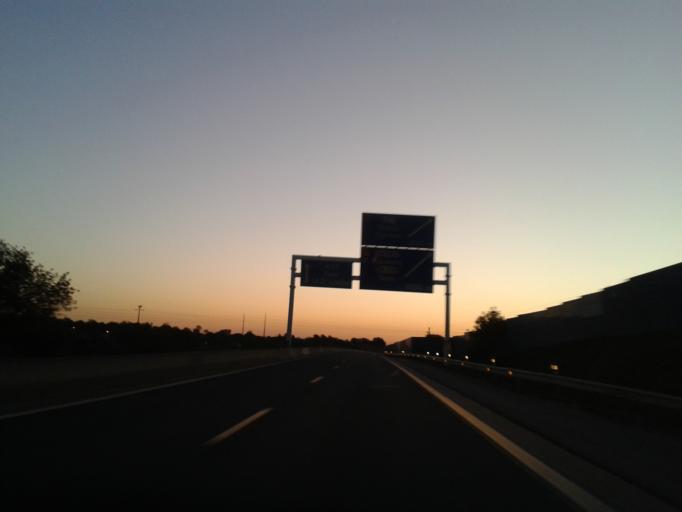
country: PT
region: Faro
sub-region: Albufeira
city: Guia
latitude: 37.1388
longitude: -8.2708
